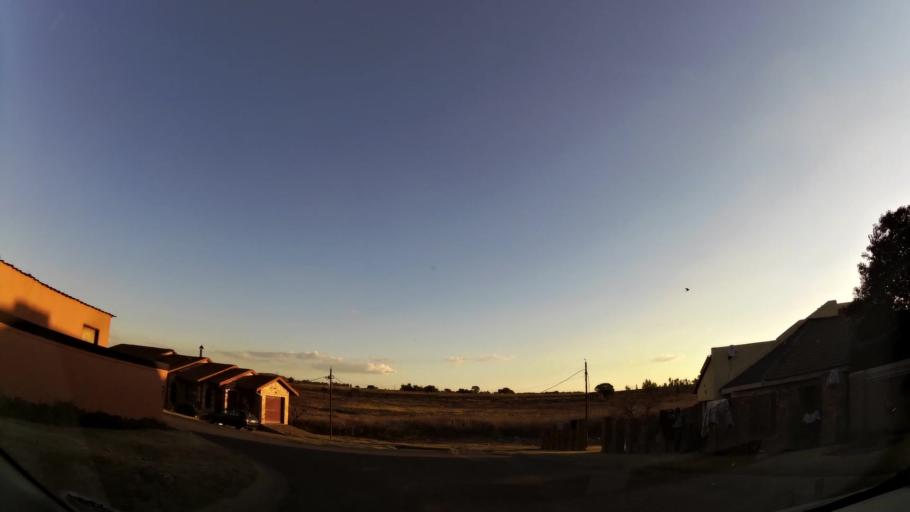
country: ZA
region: Mpumalanga
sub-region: Nkangala District Municipality
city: Witbank
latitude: -25.8845
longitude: 29.1792
